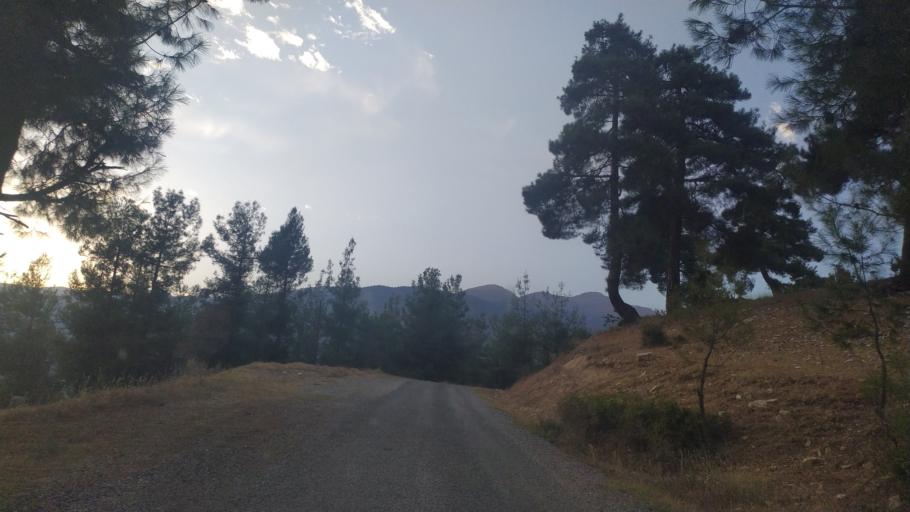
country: TR
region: Mersin
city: Camliyayla
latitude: 37.2219
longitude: 34.7107
